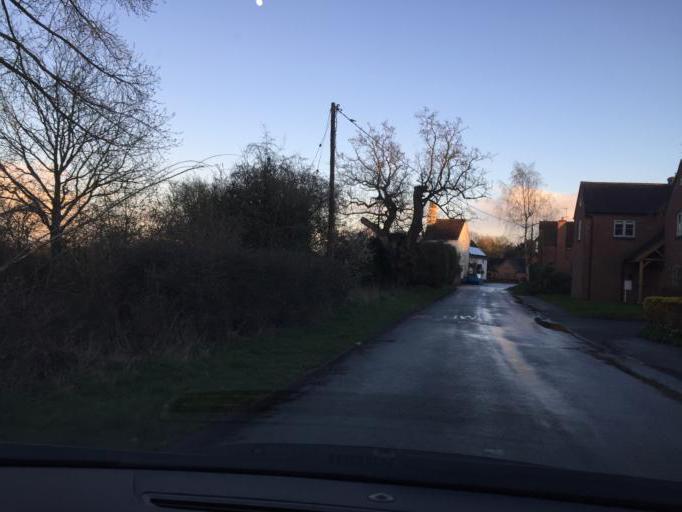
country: GB
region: England
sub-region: Warwickshire
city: Wroxall
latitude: 52.2674
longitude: -1.6698
